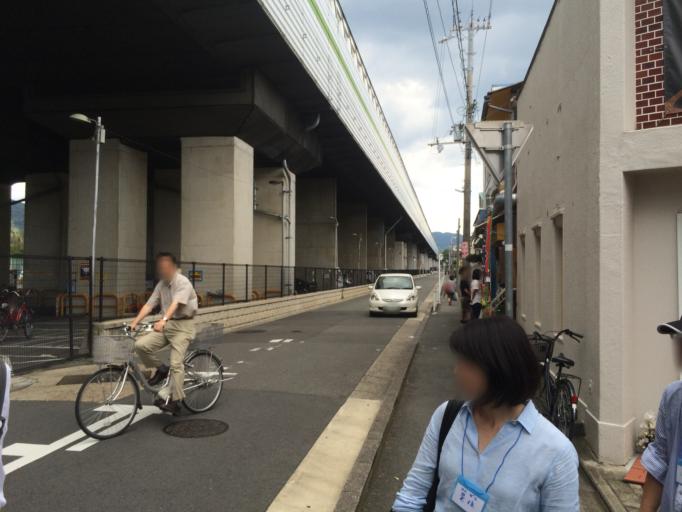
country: JP
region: Kyoto
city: Kyoto
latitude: 34.9565
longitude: 135.7713
